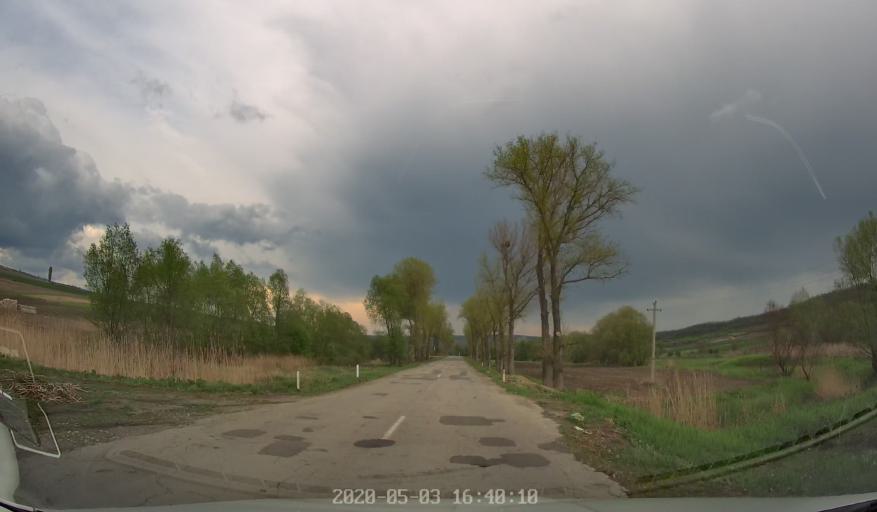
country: MD
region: Stinga Nistrului
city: Bucovat
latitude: 47.1771
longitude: 28.3872
